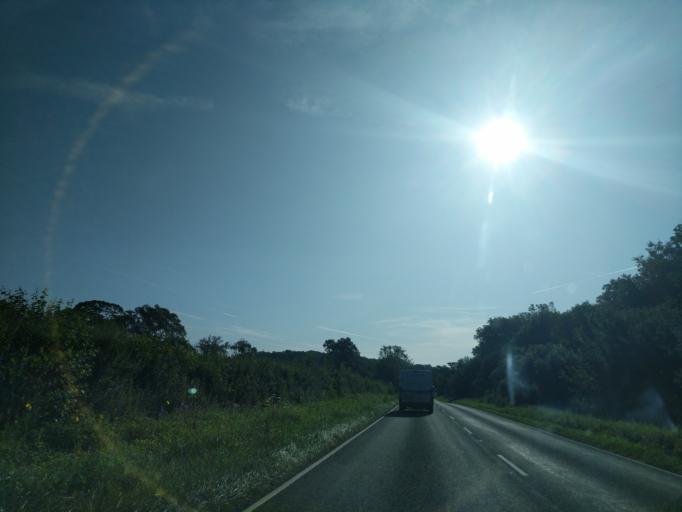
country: GB
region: England
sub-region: District of Rutland
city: Clipsham
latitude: 52.8032
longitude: -0.5841
